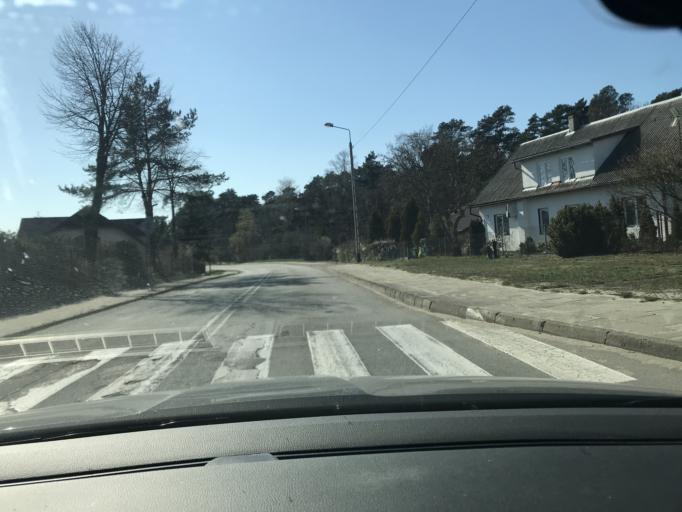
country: PL
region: Pomeranian Voivodeship
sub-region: Powiat nowodworski
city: Sztutowo
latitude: 54.3370
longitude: 19.2206
